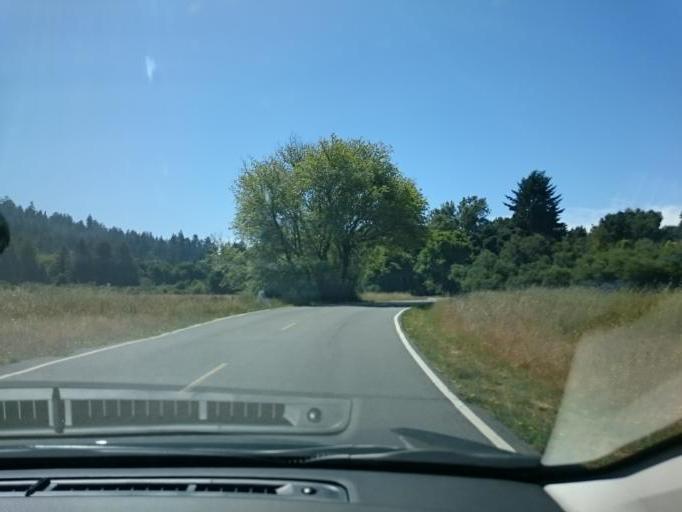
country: US
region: California
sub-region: Santa Cruz County
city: Felton
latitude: 37.0430
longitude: -122.0662
